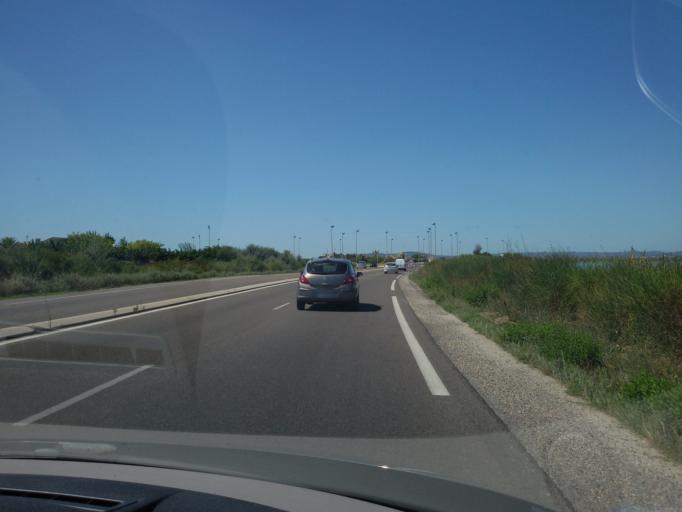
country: FR
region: Languedoc-Roussillon
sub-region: Departement de l'Herault
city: Palavas-les-Flots
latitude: 43.5346
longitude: 3.9415
